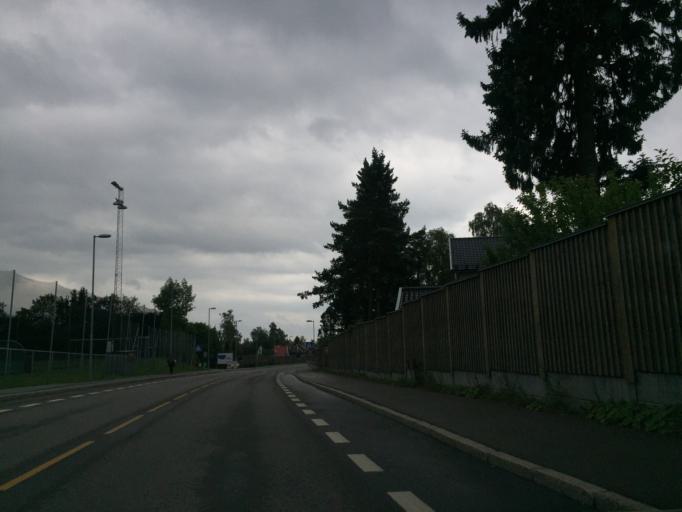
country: NO
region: Oslo
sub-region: Oslo
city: Sjolyststranda
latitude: 59.9503
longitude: 10.6755
